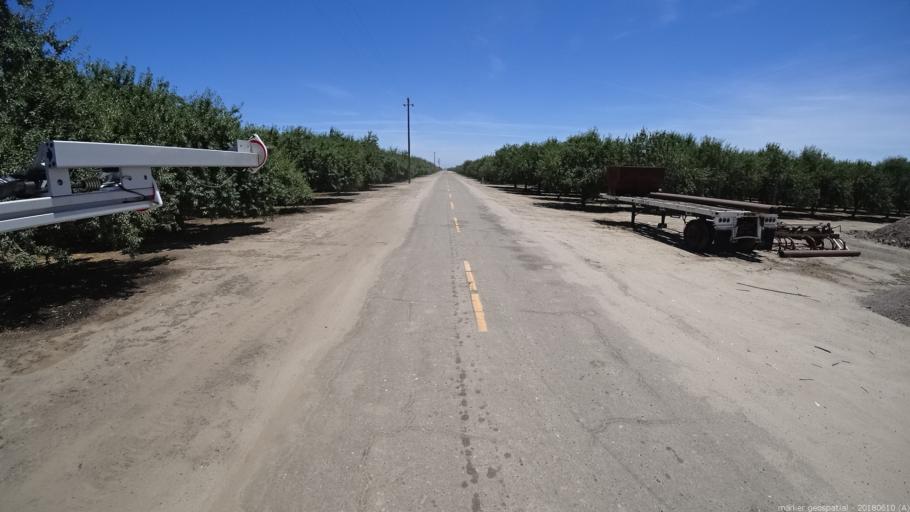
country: US
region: California
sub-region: Madera County
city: Chowchilla
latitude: 37.0473
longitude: -120.2823
